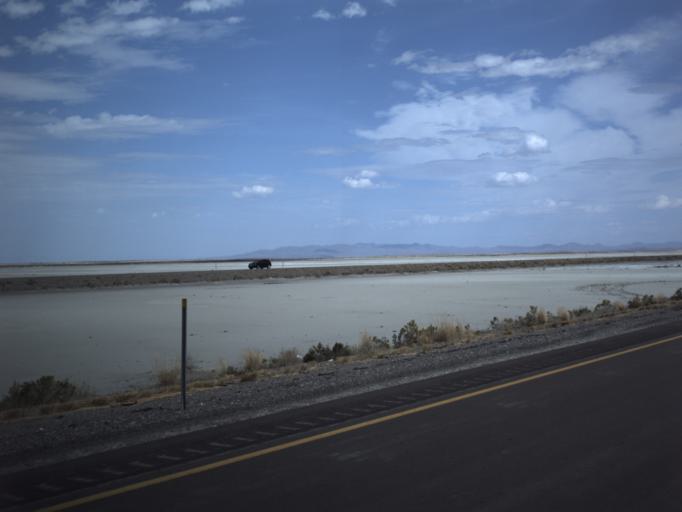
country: US
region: Utah
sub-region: Tooele County
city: Wendover
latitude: 40.7302
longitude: -113.4704
